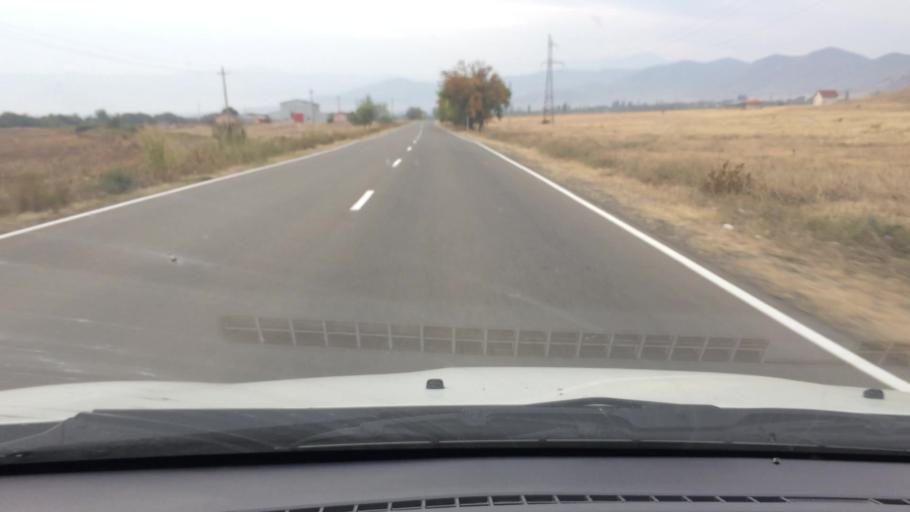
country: GE
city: Naghvarevi
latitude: 41.3418
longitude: 44.8127
